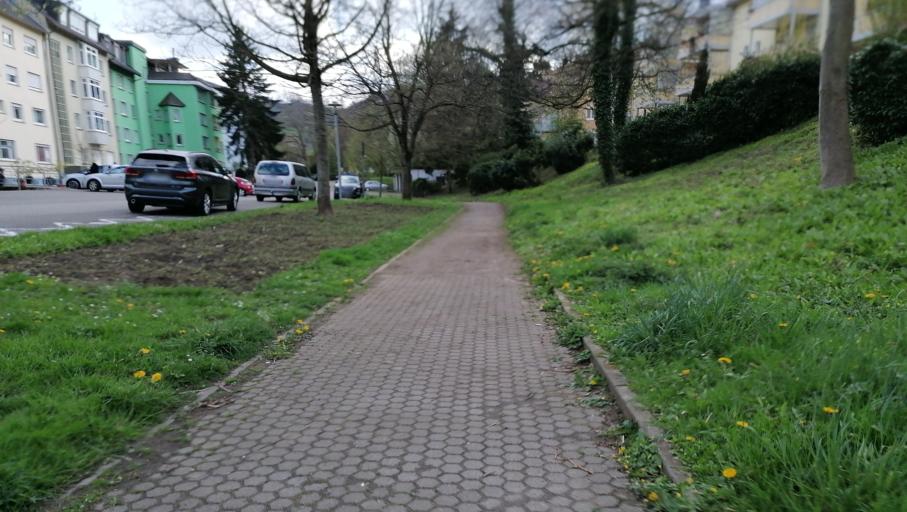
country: DE
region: Baden-Wuerttemberg
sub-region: Freiburg Region
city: Bad Sackingen
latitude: 47.5520
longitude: 7.9449
